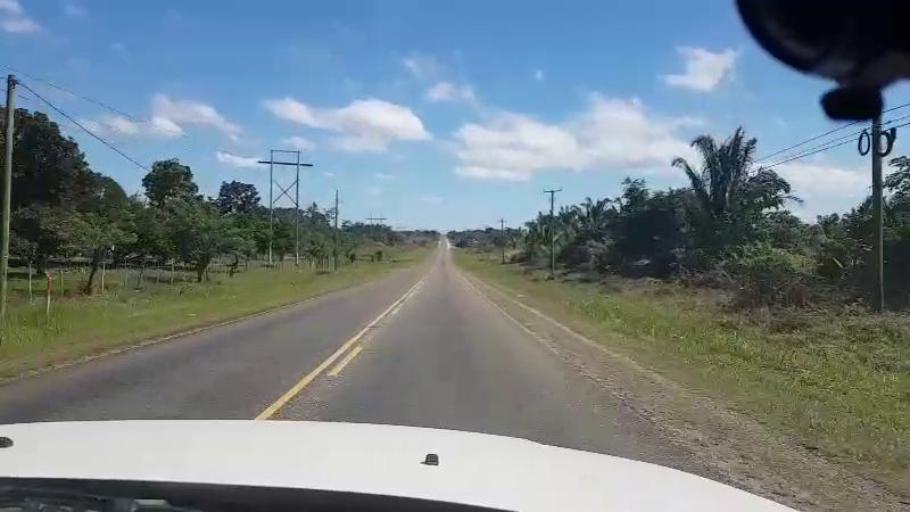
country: BZ
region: Cayo
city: Belmopan
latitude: 17.2768
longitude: -88.7263
